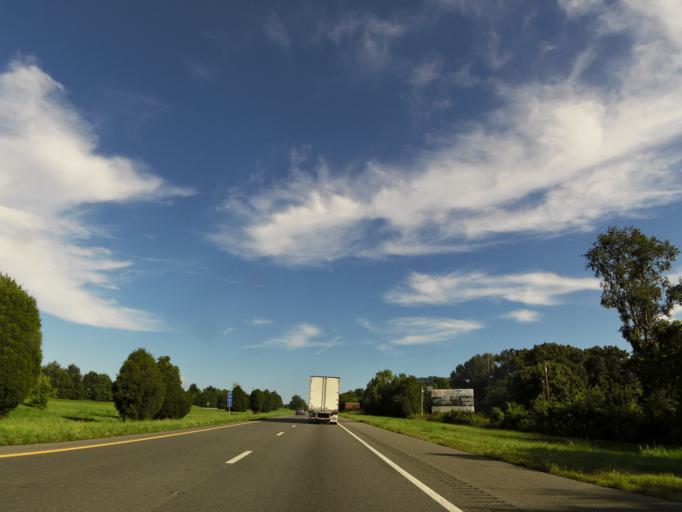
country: US
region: Tennessee
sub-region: Montgomery County
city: Clarksville
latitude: 36.6119
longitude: -87.2936
